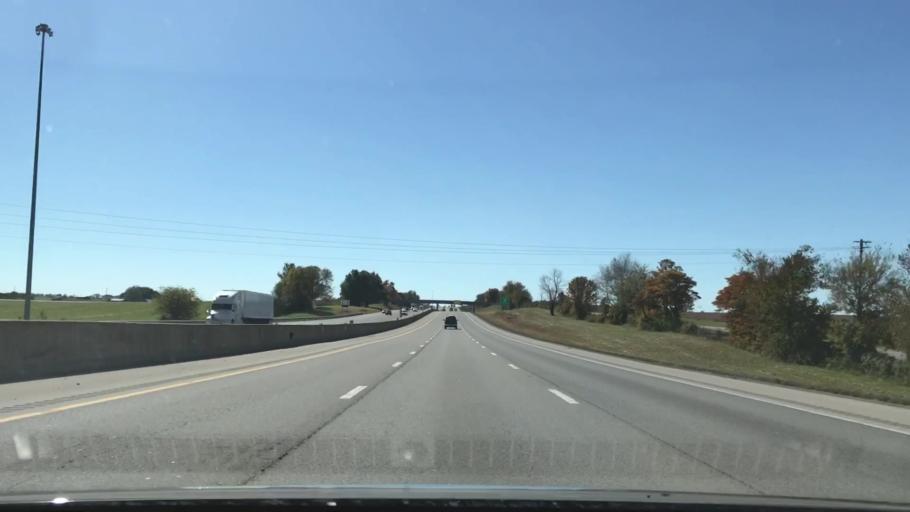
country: US
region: Kentucky
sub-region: Simpson County
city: Franklin
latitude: 36.6831
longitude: -86.5417
